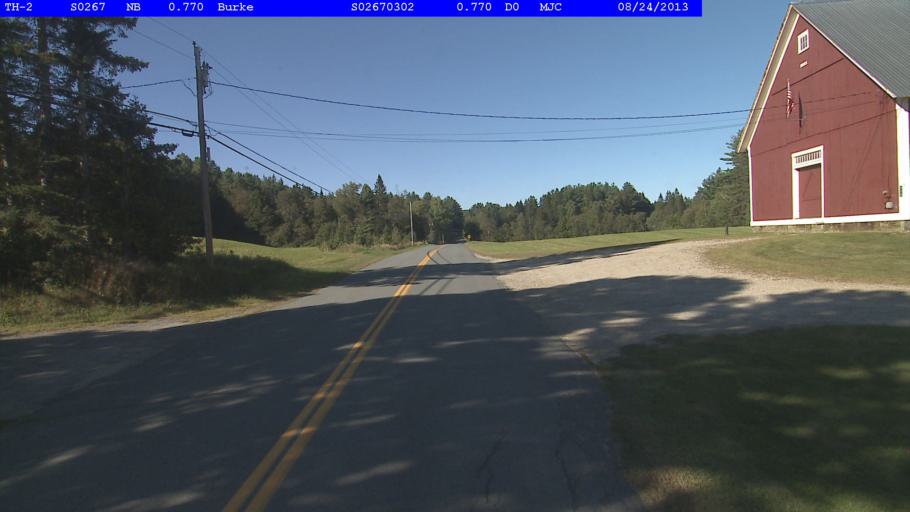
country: US
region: Vermont
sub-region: Caledonia County
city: Lyndonville
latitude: 44.5978
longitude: -71.9420
